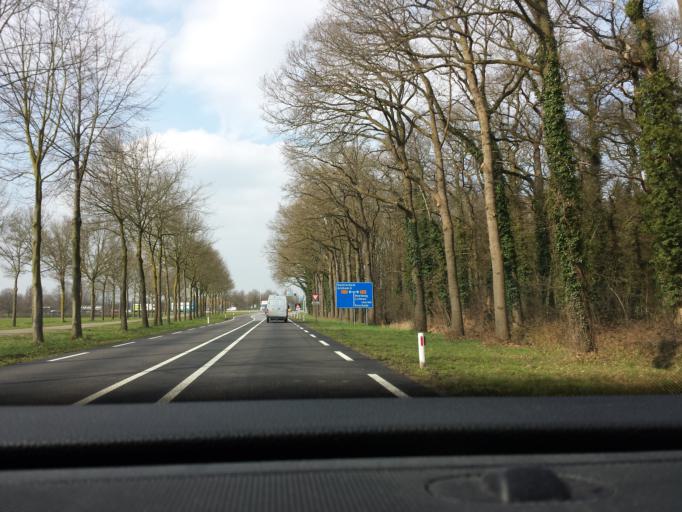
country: NL
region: Gelderland
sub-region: Oude IJsselstreek
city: Varsseveld
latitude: 51.9509
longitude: 6.4706
